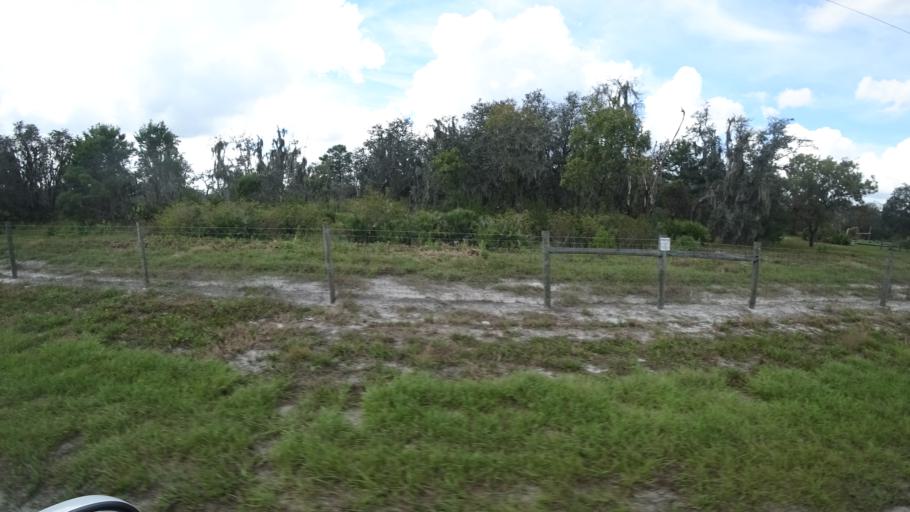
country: US
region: Florida
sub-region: Hillsborough County
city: Wimauma
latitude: 27.6275
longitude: -82.2310
